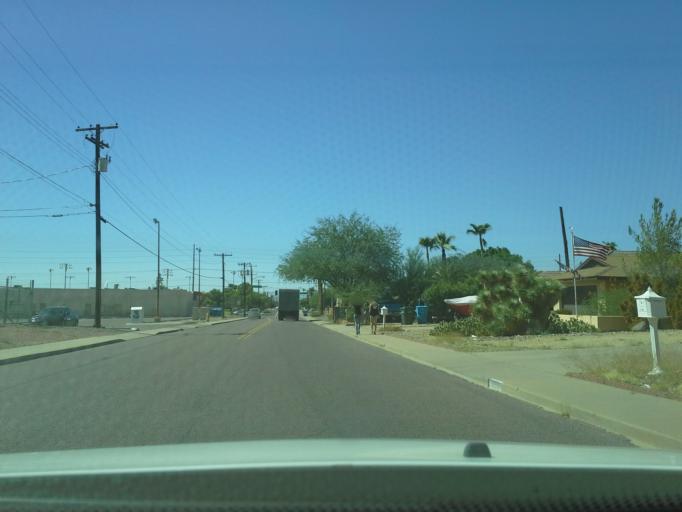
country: US
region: Arizona
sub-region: Maricopa County
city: Paradise Valley
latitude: 33.5678
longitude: -112.0548
